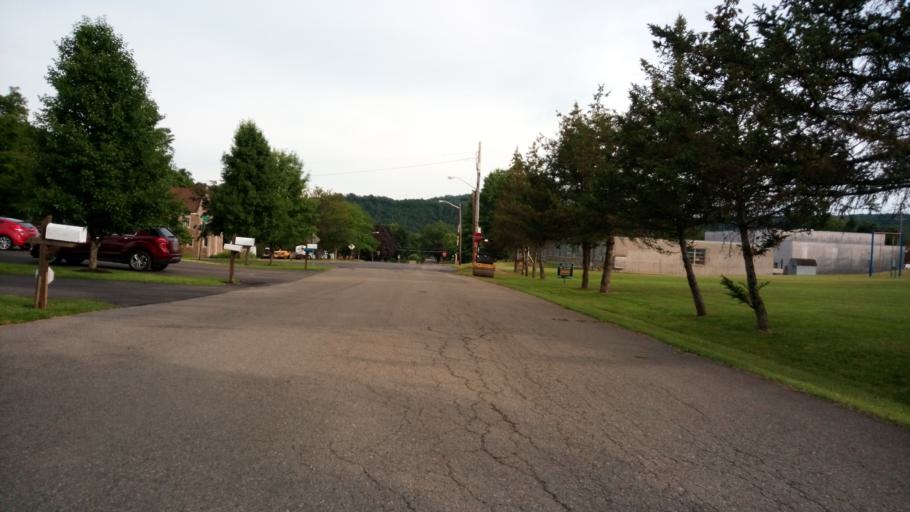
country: US
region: New York
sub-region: Chemung County
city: West Elmira
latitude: 42.0838
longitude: -76.8375
